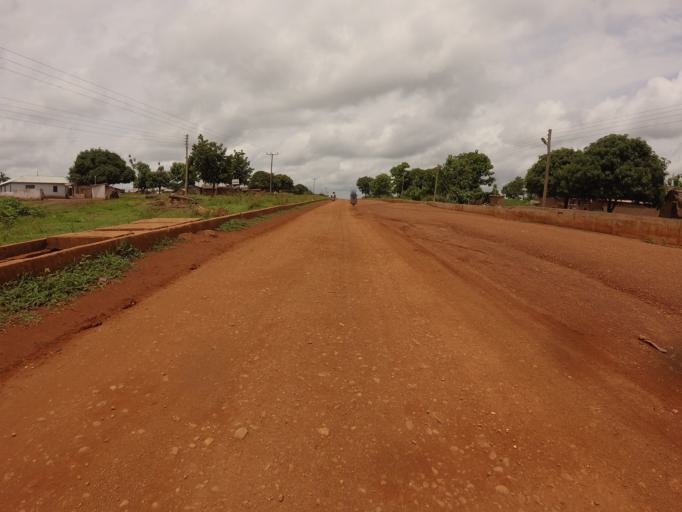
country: GH
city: Kpandae
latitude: 8.4539
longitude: 0.3459
